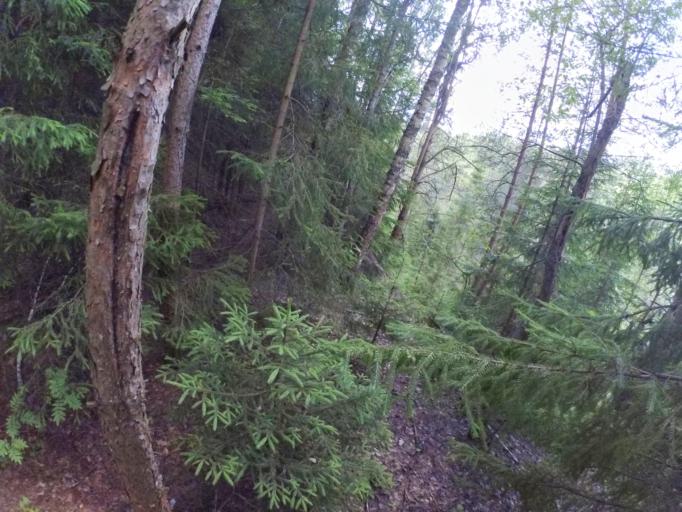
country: RU
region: Moskovskaya
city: Fosforitnyy
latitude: 55.3364
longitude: 38.9411
